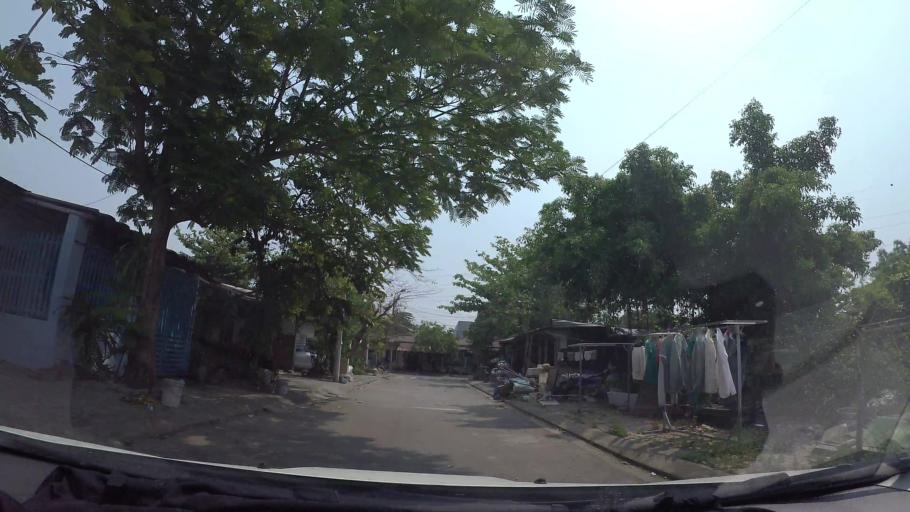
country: VN
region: Da Nang
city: Cam Le
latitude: 15.9972
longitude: 108.2063
